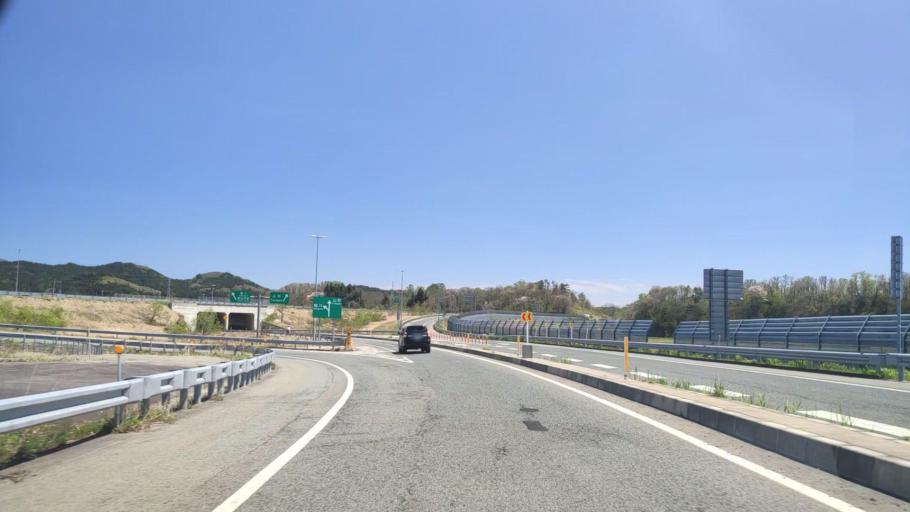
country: JP
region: Yamagata
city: Shinjo
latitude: 38.7398
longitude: 140.2962
